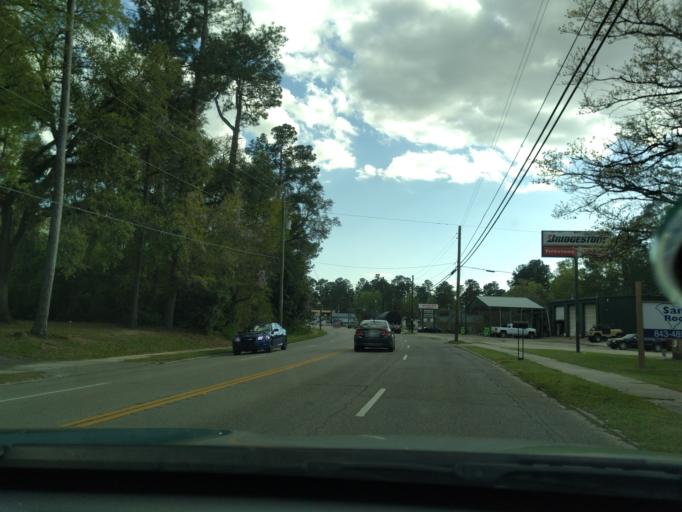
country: US
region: South Carolina
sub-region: Williamsburg County
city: Kingstree
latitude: 33.6736
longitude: -79.8354
